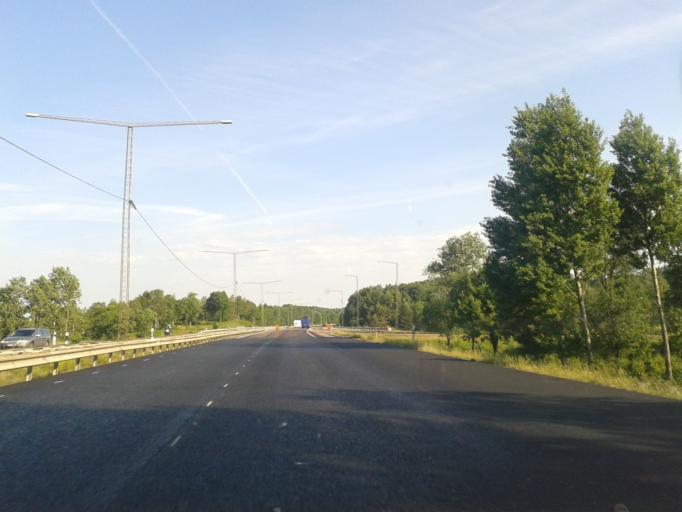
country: SE
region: Vaestra Goetaland
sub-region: Kungalvs Kommun
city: Kode
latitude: 57.9439
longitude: 11.8579
